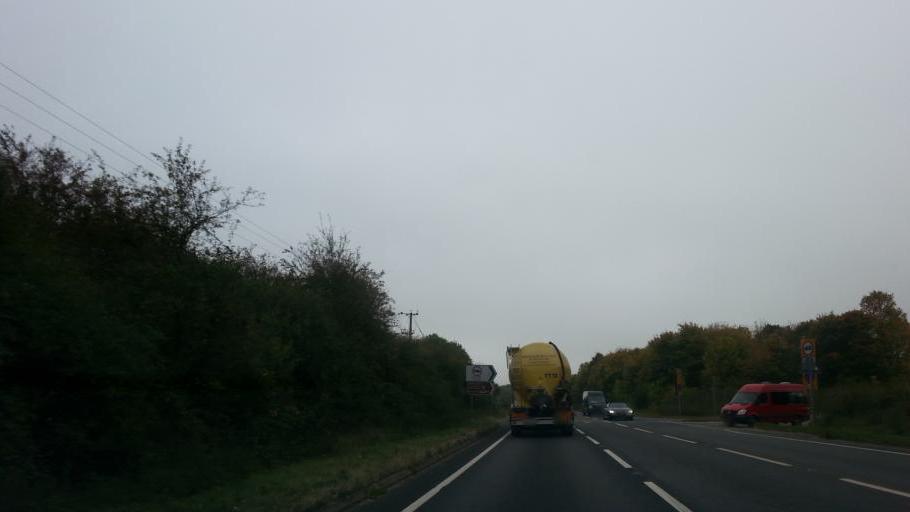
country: GB
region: England
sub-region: Northamptonshire
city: Oundle
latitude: 52.4568
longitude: -0.4626
